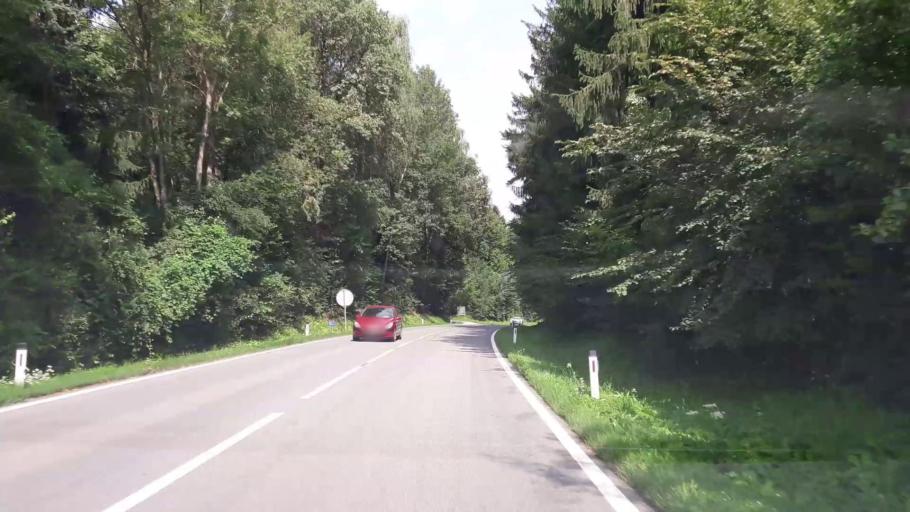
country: AT
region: Styria
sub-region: Politischer Bezirk Hartberg-Fuerstenfeld
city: Kaindorf
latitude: 47.2448
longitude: 15.9298
